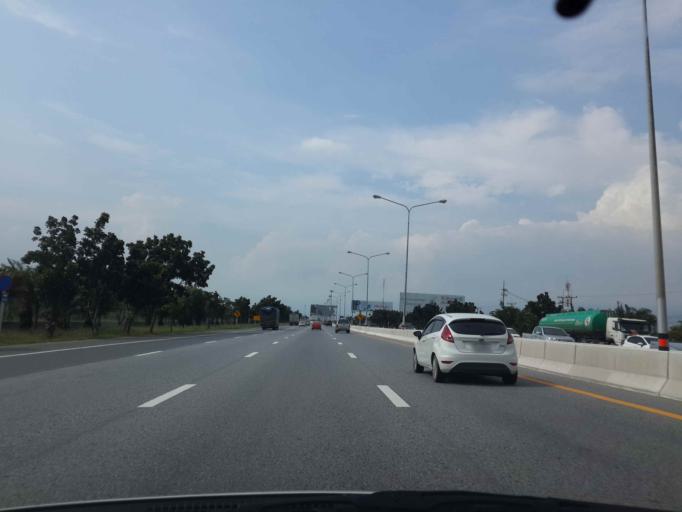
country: TH
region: Chon Buri
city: Phan Thong
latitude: 13.4856
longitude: 101.0465
